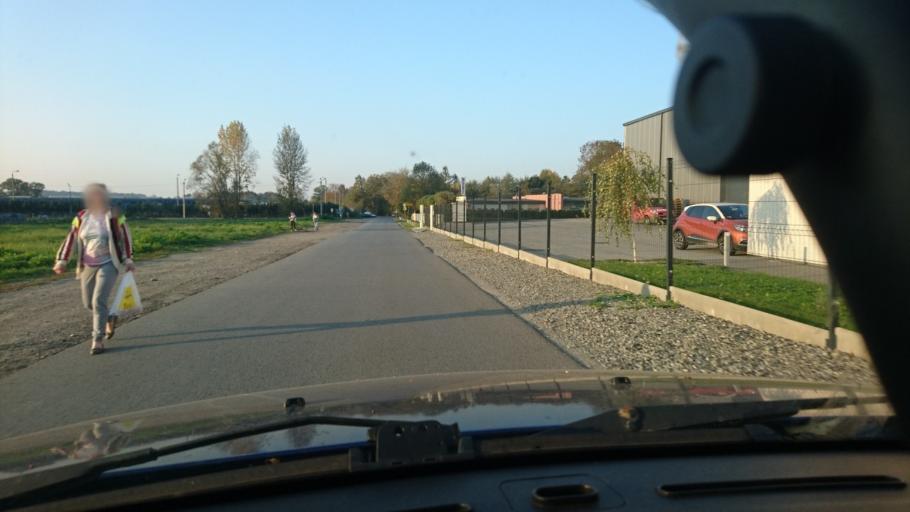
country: PL
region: Silesian Voivodeship
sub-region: Powiat bielski
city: Mazancowice
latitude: 49.8234
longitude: 18.9803
